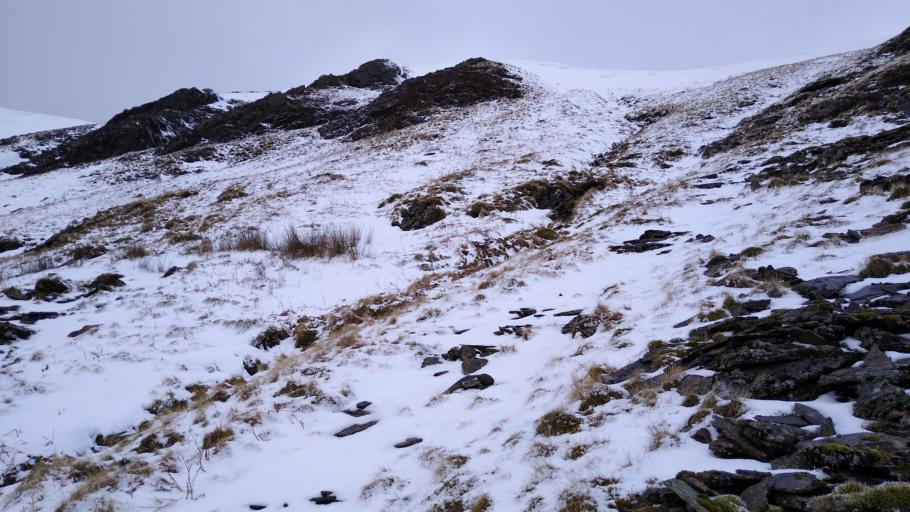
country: GB
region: England
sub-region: Cumbria
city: Keswick
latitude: 54.6611
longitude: -3.0335
